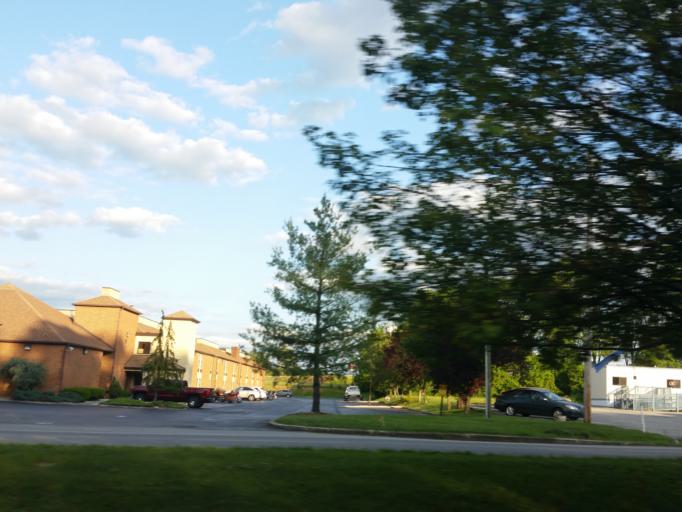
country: US
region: Virginia
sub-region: Washington County
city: Abingdon
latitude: 36.6957
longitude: -82.0108
